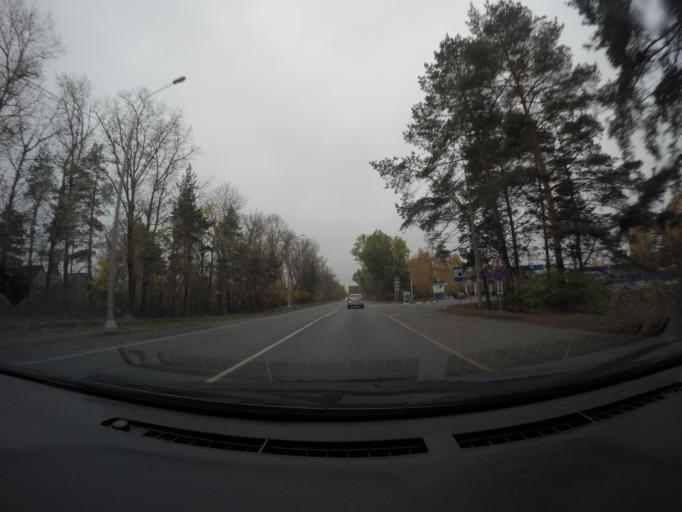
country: RU
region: Moskovskaya
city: Malyshevo
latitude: 55.4725
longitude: 38.3419
